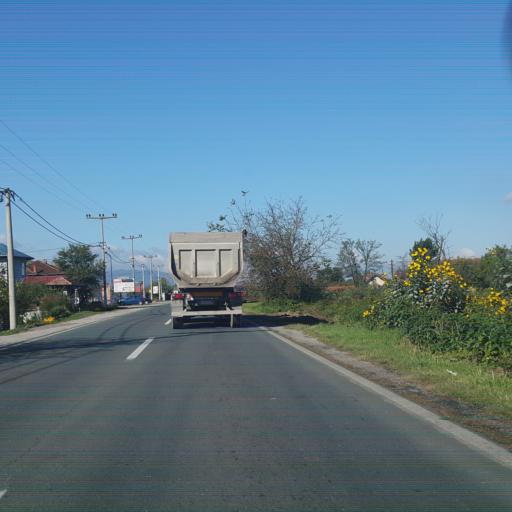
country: RS
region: Central Serbia
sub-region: Rasinski Okrug
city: Trstenik
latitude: 43.6332
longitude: 20.9559
